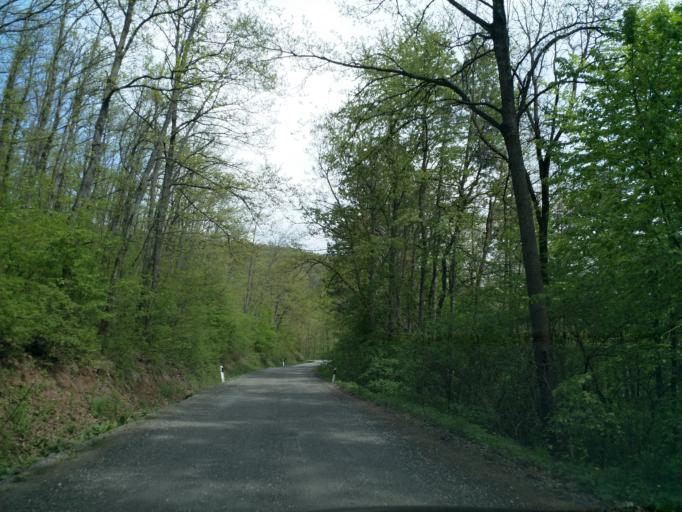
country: RS
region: Central Serbia
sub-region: Pomoravski Okrug
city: Despotovac
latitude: 43.9689
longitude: 21.5529
